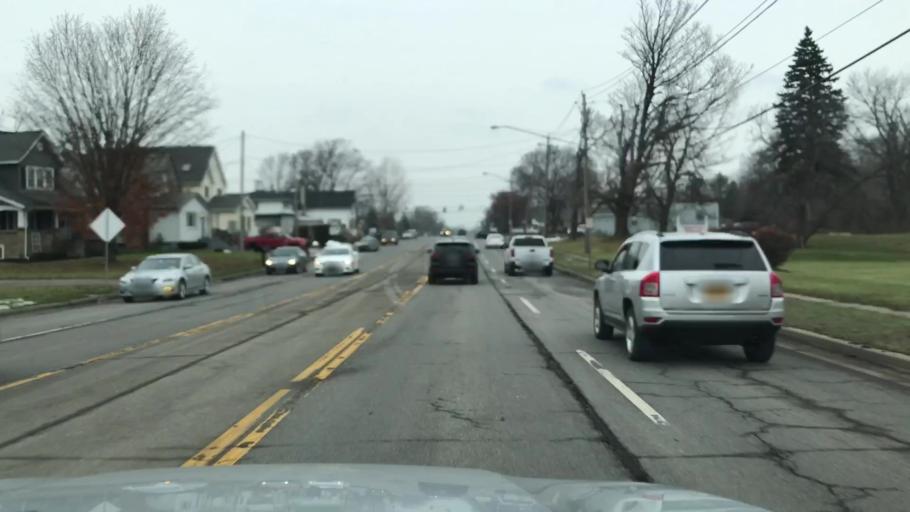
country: US
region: New York
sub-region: Erie County
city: Blasdell
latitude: 42.8032
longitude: -78.7969
